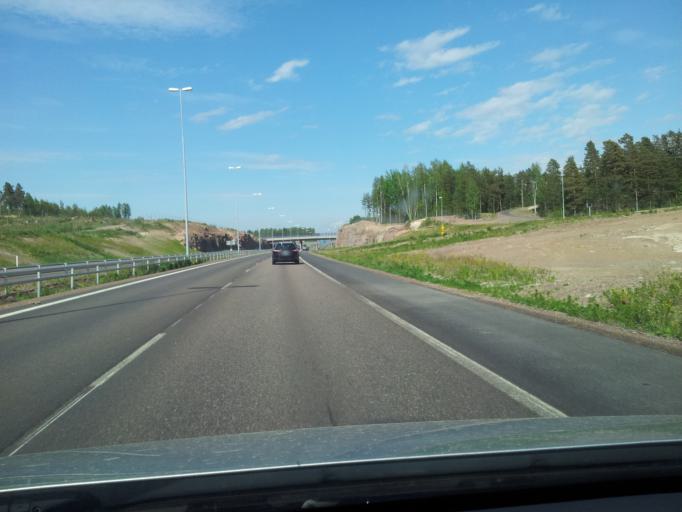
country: FI
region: Kymenlaakso
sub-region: Kotka-Hamina
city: Hamina
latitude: 60.5869
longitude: 27.1540
